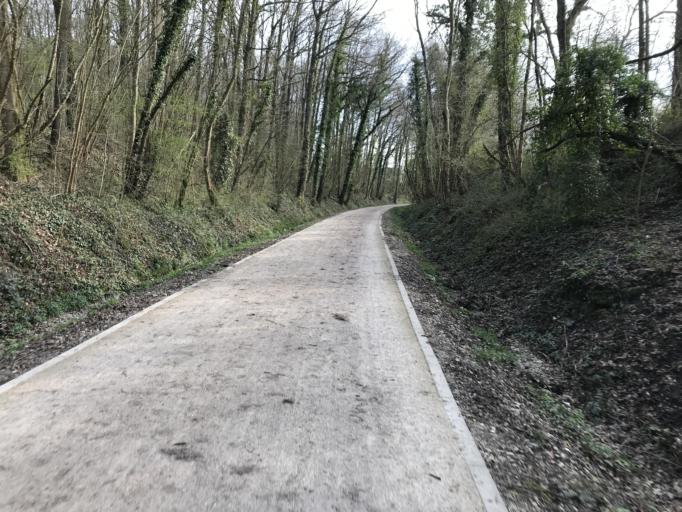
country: FR
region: Ile-de-France
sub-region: Departement de l'Essonne
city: Les Molieres
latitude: 48.6725
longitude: 2.0536
